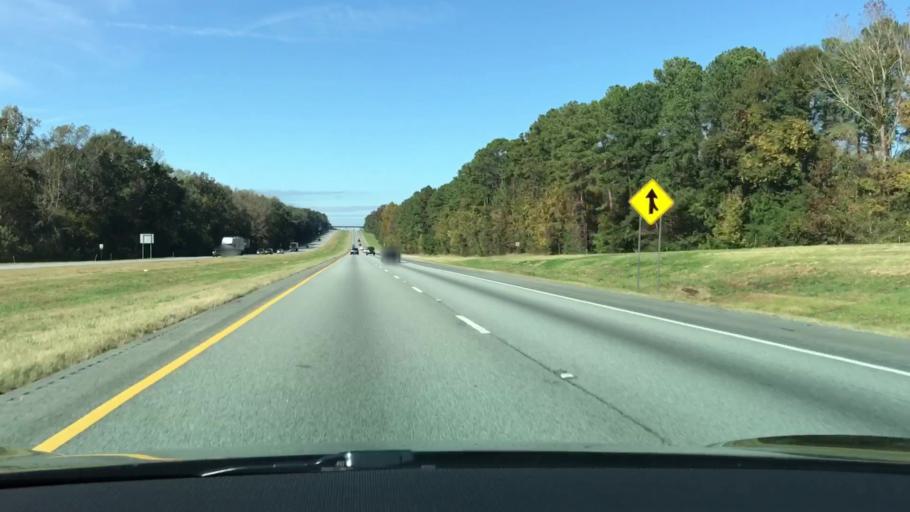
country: US
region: Georgia
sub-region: Morgan County
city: Madison
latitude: 33.5625
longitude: -83.5016
